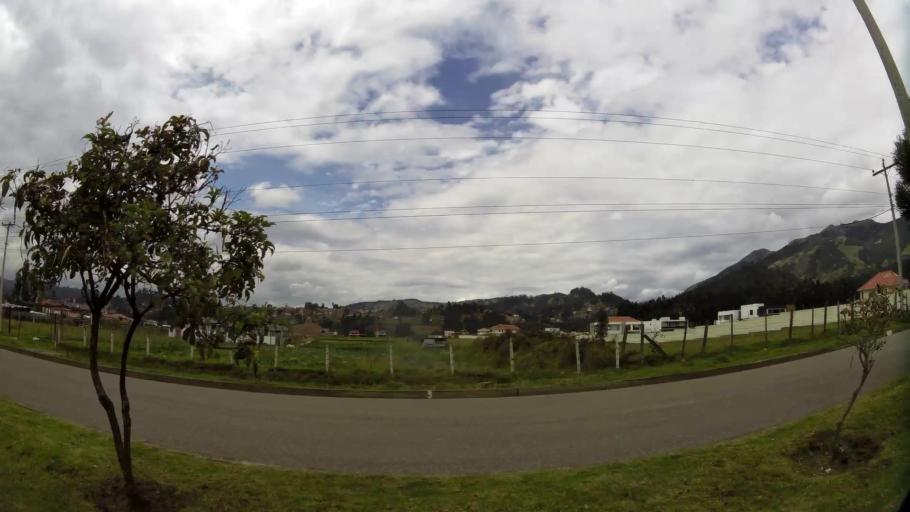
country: EC
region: Azuay
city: Cuenca
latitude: -2.8919
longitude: -79.0566
